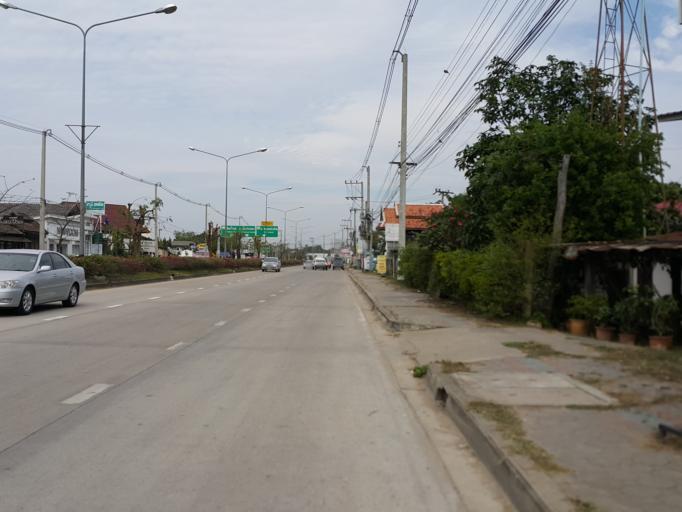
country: TH
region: Chiang Mai
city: Saraphi
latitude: 18.7731
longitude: 99.0417
